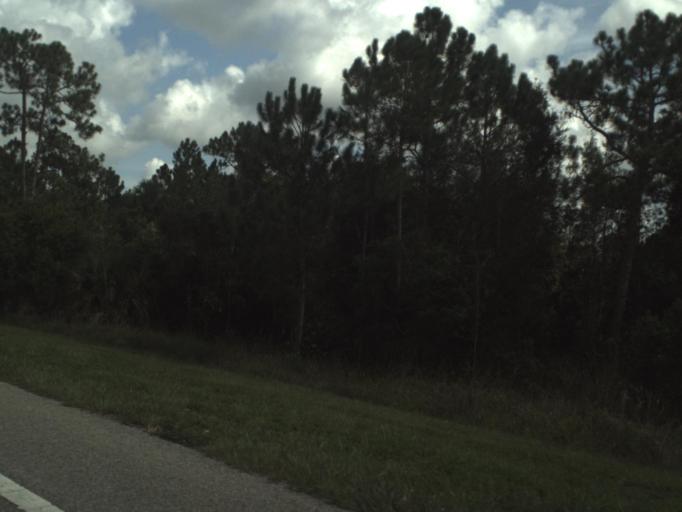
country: US
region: Florida
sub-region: Palm Beach County
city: Limestone Creek
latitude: 26.9000
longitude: -80.2849
